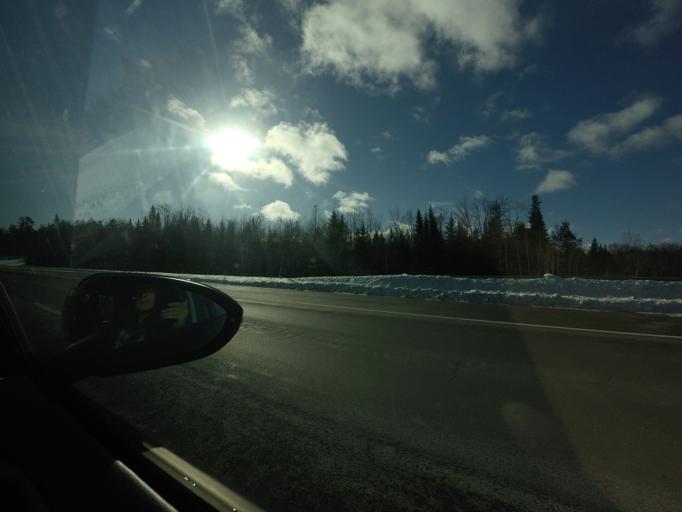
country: CA
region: New Brunswick
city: Fredericton
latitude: 45.8769
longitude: -66.6322
